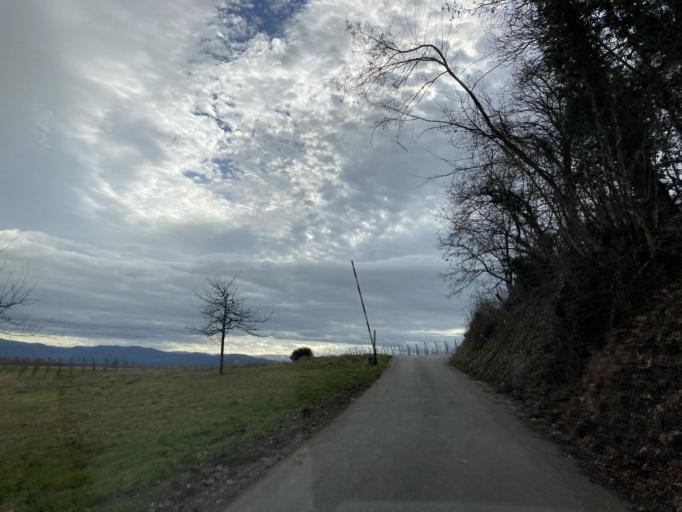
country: DE
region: Baden-Wuerttemberg
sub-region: Freiburg Region
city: Endingen
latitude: 48.1208
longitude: 7.7128
